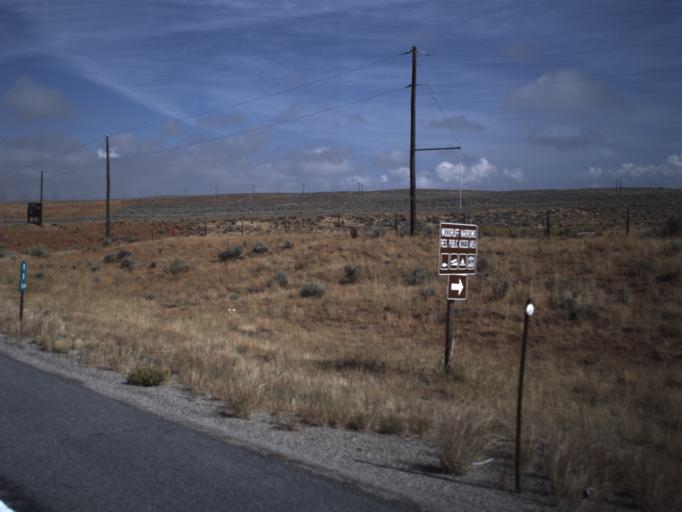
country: US
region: Wyoming
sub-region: Uinta County
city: Evanston
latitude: 41.4138
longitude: -111.0459
